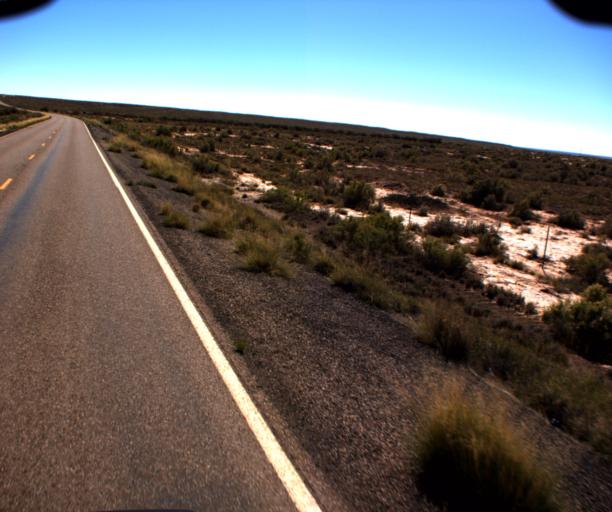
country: US
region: Arizona
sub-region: Navajo County
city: Holbrook
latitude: 35.0557
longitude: -110.0961
